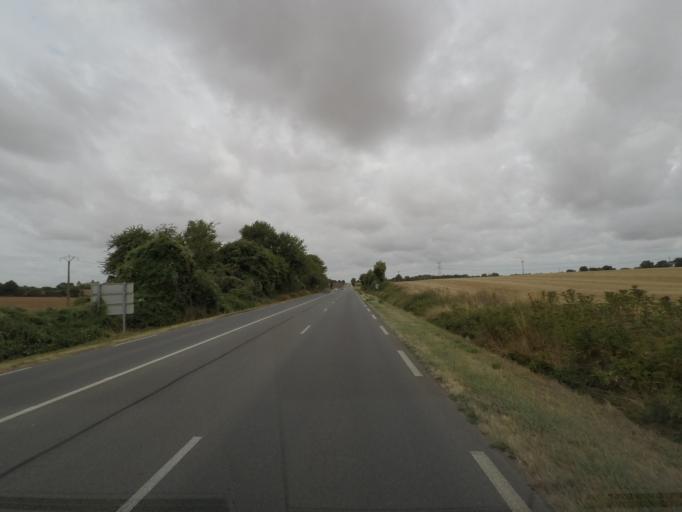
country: FR
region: Poitou-Charentes
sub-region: Departement des Deux-Sevres
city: Celles-sur-Belle
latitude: 46.2705
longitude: -0.2303
